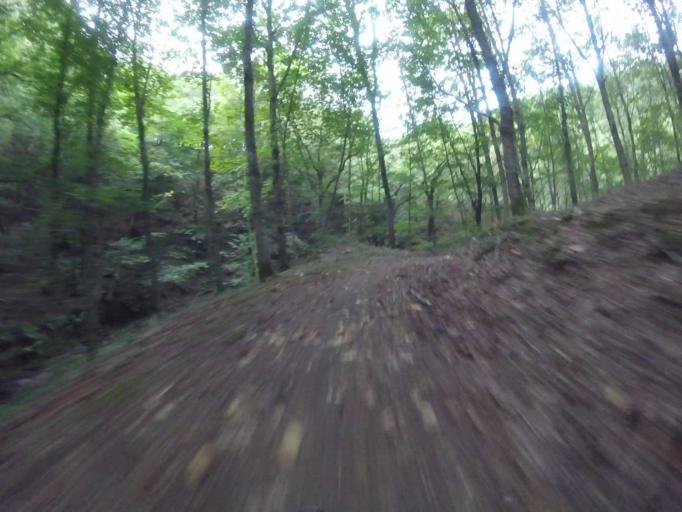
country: ES
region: Basque Country
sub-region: Provincia de Guipuzcoa
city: Errenteria
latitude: 43.2737
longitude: -1.8421
